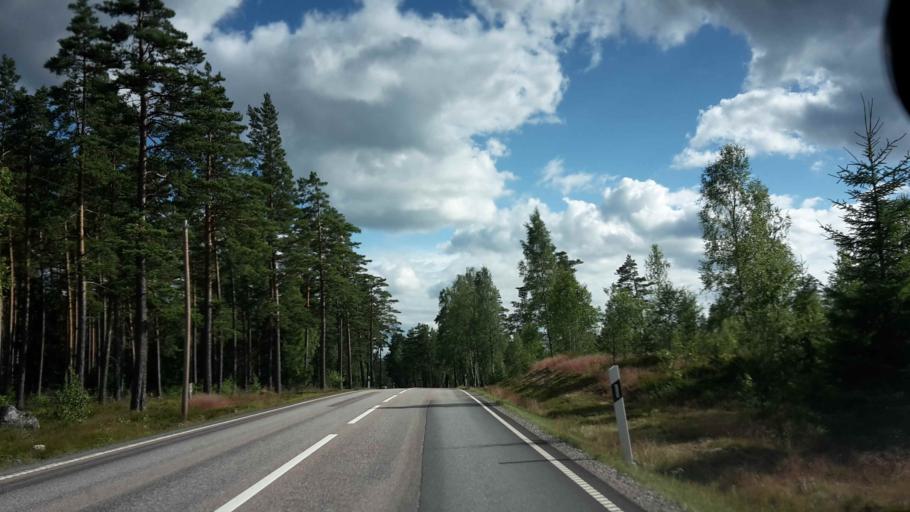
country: SE
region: OErebro
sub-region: Hallsbergs Kommun
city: Palsboda
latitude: 58.8479
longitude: 15.4043
